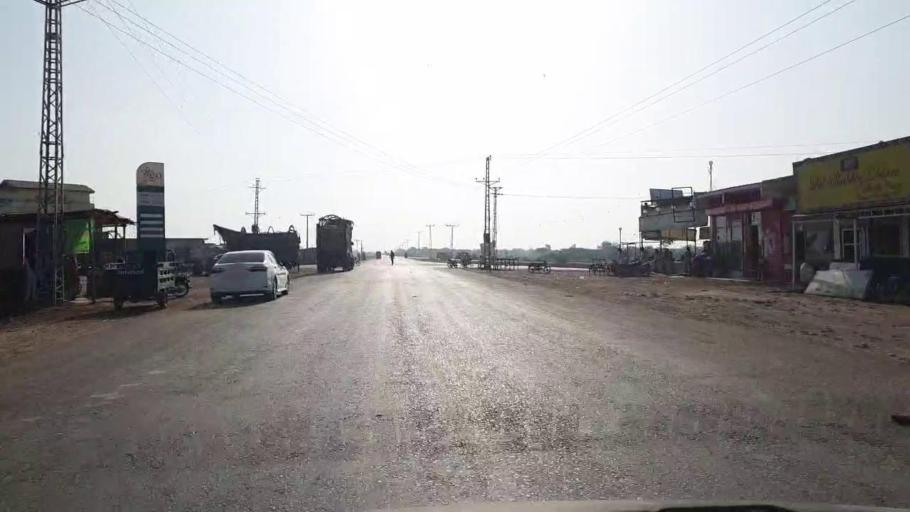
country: PK
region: Sindh
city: Badin
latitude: 24.6665
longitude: 68.8677
